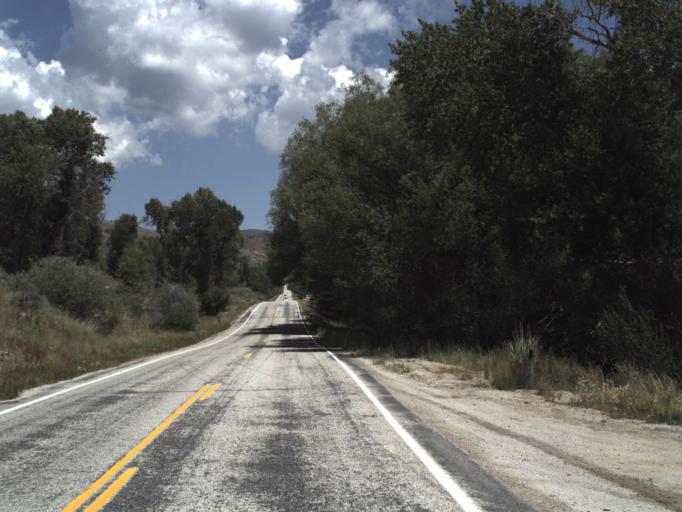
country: US
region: Utah
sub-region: Weber County
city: Wolf Creek
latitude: 41.2870
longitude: -111.6463
